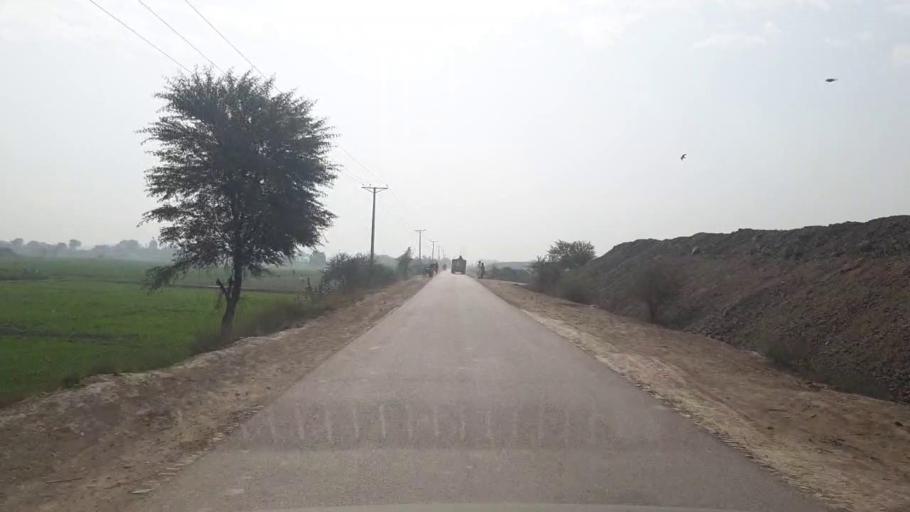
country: PK
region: Sindh
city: Hala
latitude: 25.7681
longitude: 68.4467
